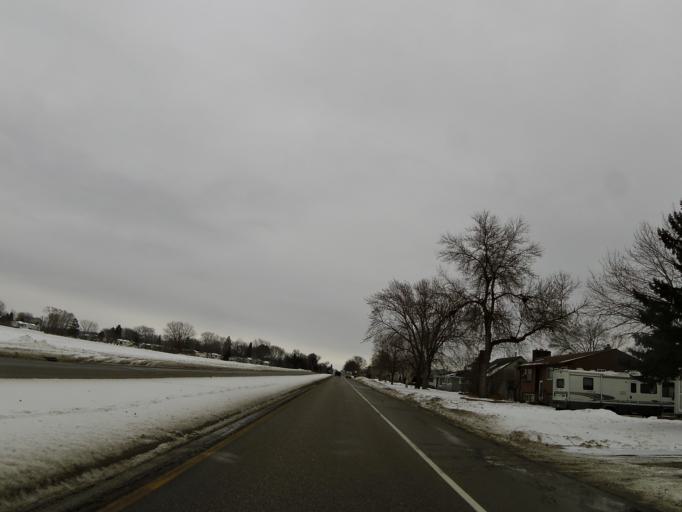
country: US
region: Minnesota
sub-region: Dakota County
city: Inver Grove Heights
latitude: 44.8480
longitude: -93.0318
